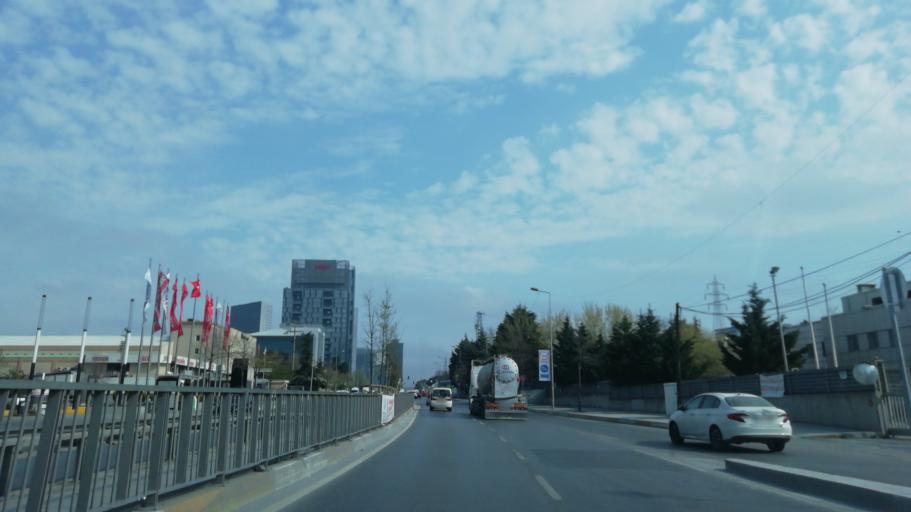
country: TR
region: Istanbul
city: Mahmutbey
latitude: 41.0472
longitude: 28.8122
